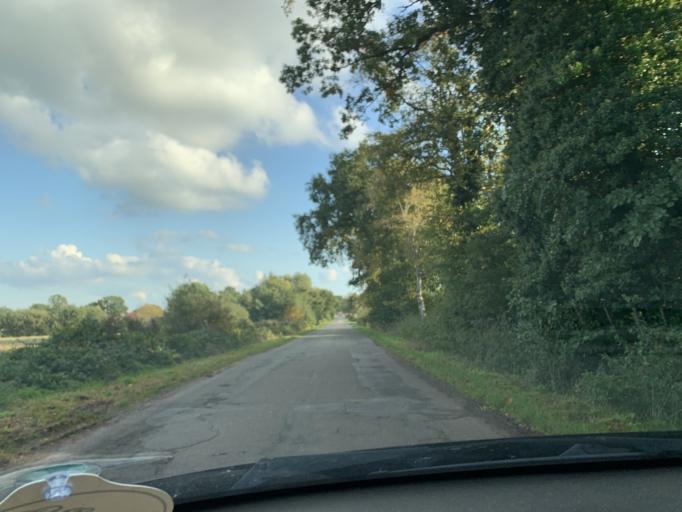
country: DE
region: Lower Saxony
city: Apen
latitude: 53.2483
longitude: 7.7770
